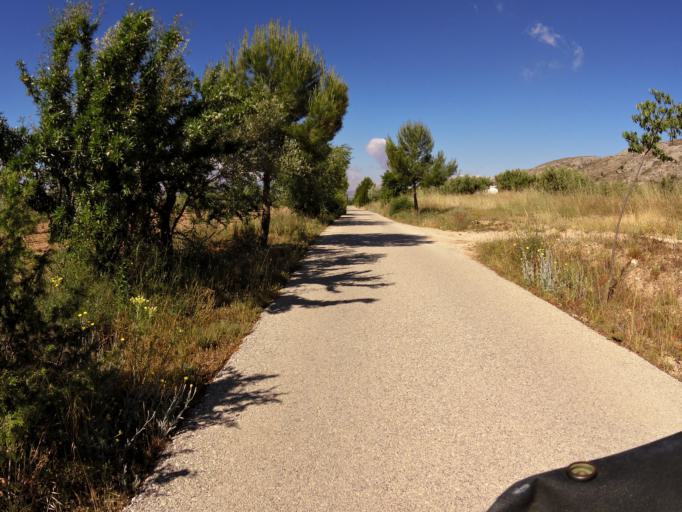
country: ES
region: Valencia
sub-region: Provincia de Alicante
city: Canada
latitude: 38.6418
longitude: -0.8175
